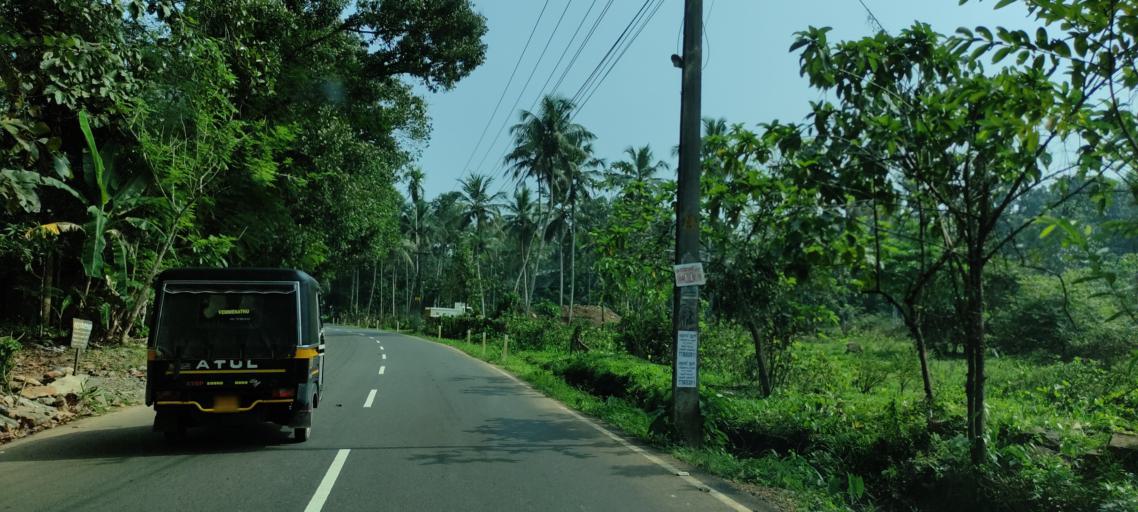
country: IN
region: Kerala
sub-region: Pattanamtitta
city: Adur
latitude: 9.2298
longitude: 76.7001
